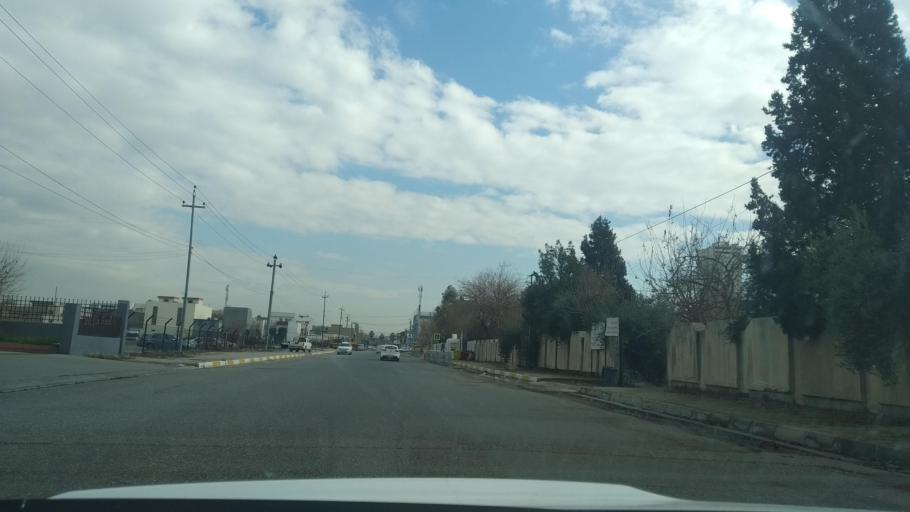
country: IQ
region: Arbil
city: Erbil
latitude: 36.1849
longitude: 43.9880
